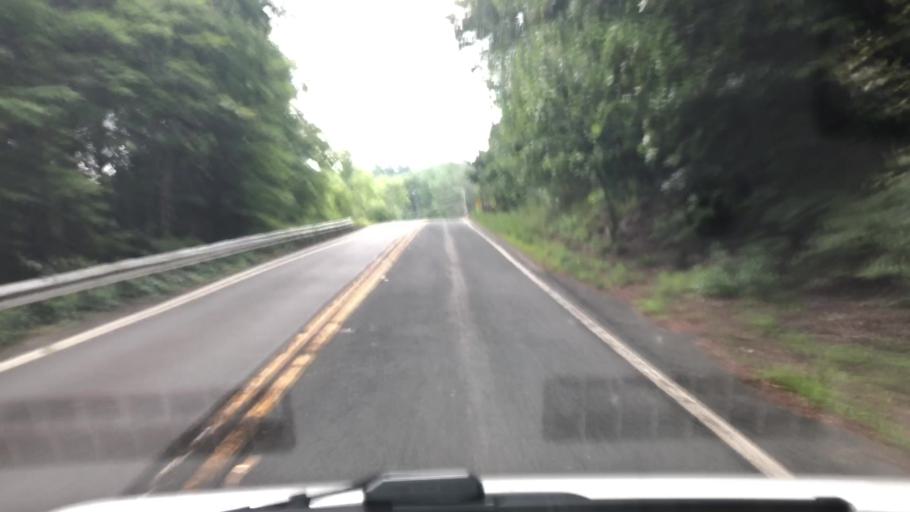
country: US
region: Massachusetts
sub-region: Franklin County
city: Conway
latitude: 42.5089
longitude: -72.6800
